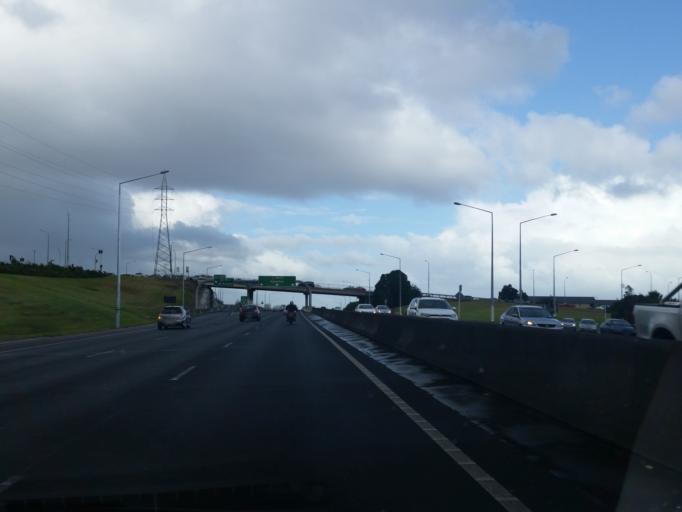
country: NZ
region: Auckland
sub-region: Auckland
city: Manukau City
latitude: -36.9903
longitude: 174.8869
